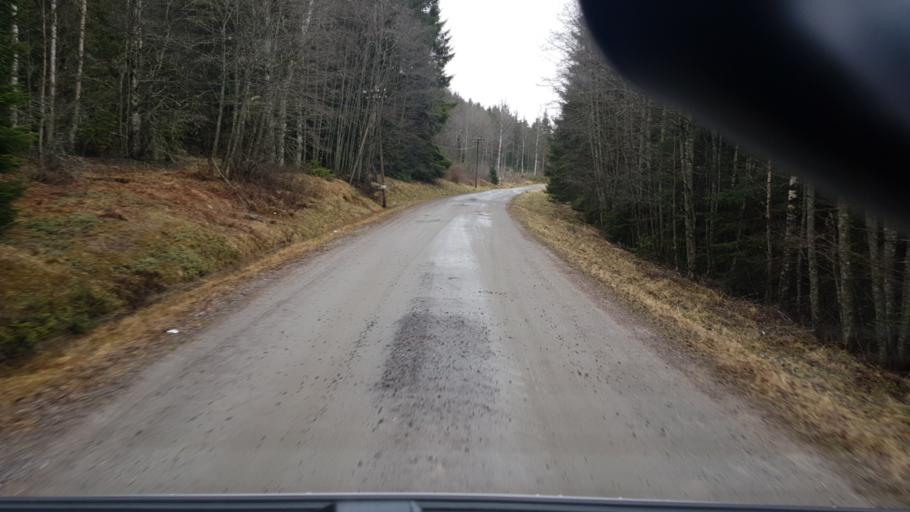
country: SE
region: Vaermland
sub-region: Eda Kommun
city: Charlottenberg
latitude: 59.9329
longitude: 12.3714
